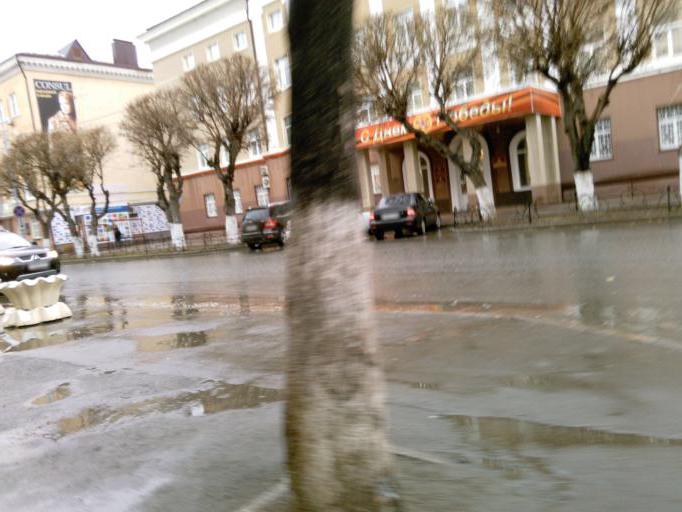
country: RU
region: Tjumen
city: Tyumen
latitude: 57.1525
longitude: 65.5447
